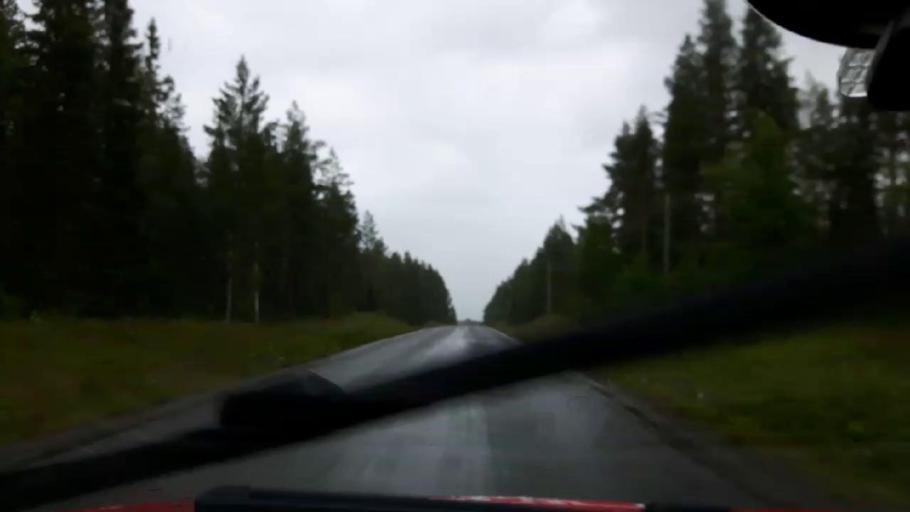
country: SE
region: Jaemtland
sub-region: OEstersunds Kommun
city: Brunflo
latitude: 62.9991
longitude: 14.7576
